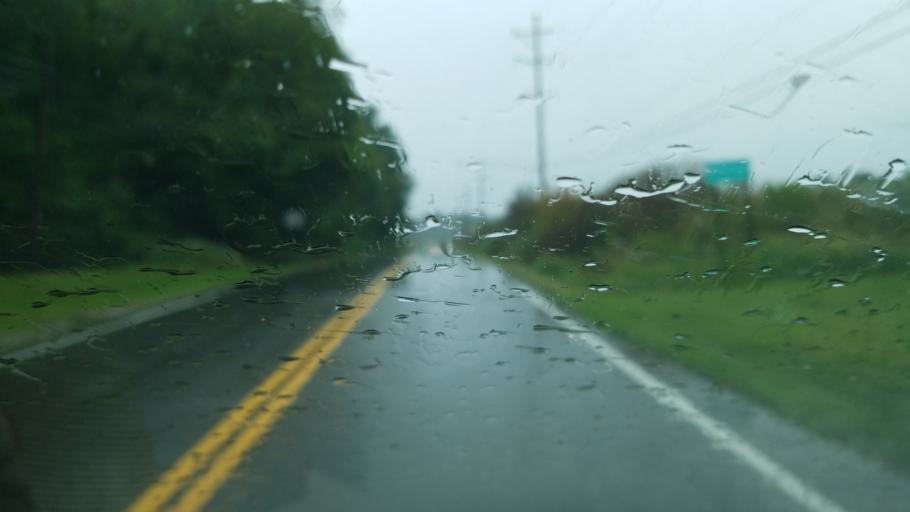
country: US
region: Ohio
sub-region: Richland County
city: Mansfield
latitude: 40.7178
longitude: -82.5121
